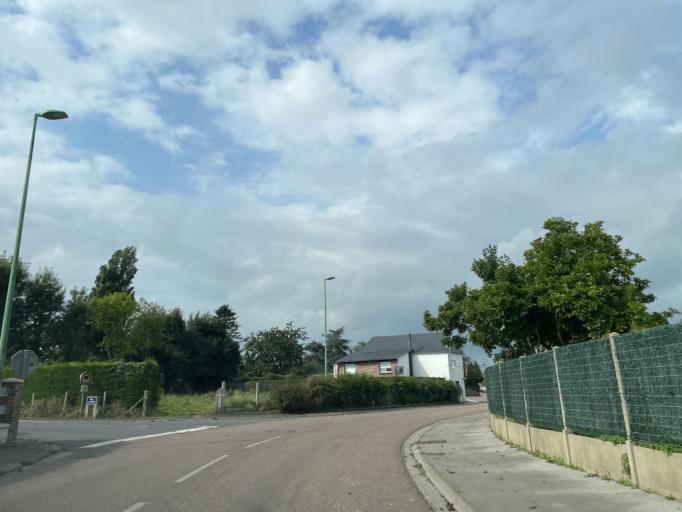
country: FR
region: Haute-Normandie
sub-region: Departement de la Seine-Maritime
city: Saint-Martin-en-Campagne
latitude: 49.9561
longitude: 1.2246
